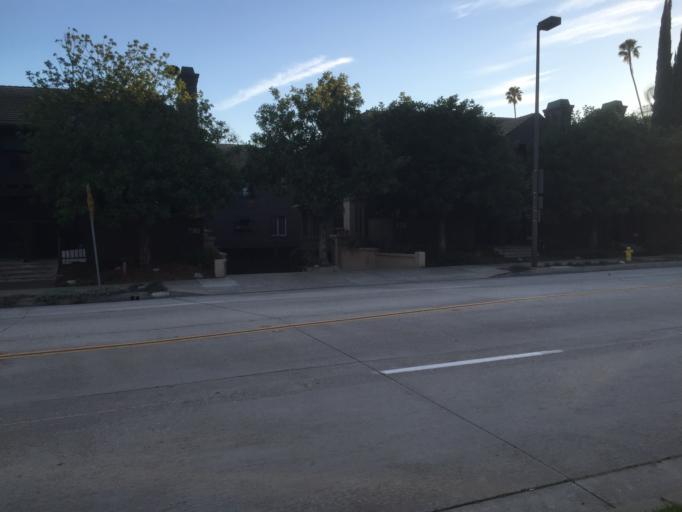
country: US
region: California
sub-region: Los Angeles County
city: Pasadena
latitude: 34.1360
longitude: -118.1344
